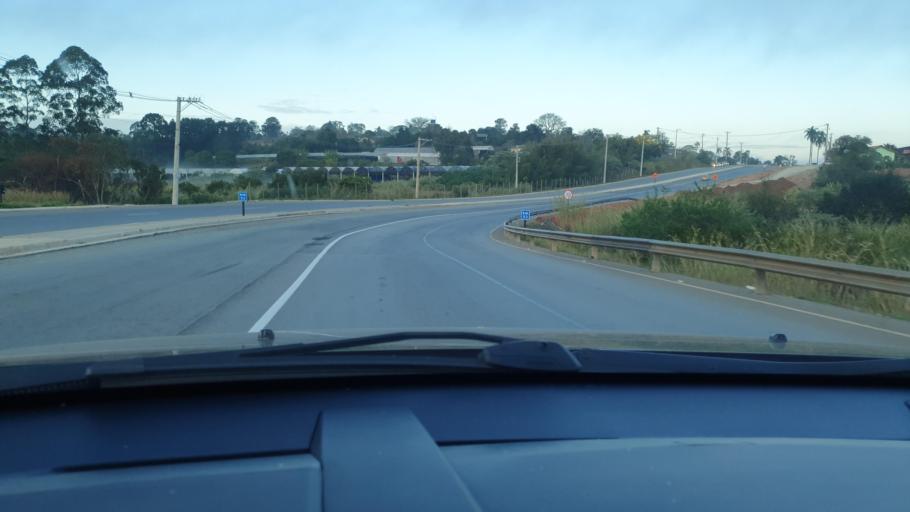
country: BR
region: Sao Paulo
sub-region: Vargem Grande Paulista
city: Vargem Grande Paulista
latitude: -23.6546
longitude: -47.0750
